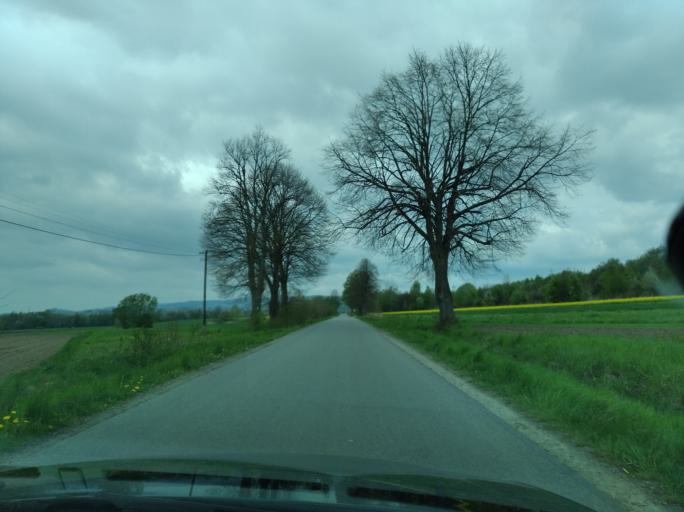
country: PL
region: Subcarpathian Voivodeship
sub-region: Powiat brzozowski
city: Jablonica Polska
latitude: 49.6862
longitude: 21.8945
